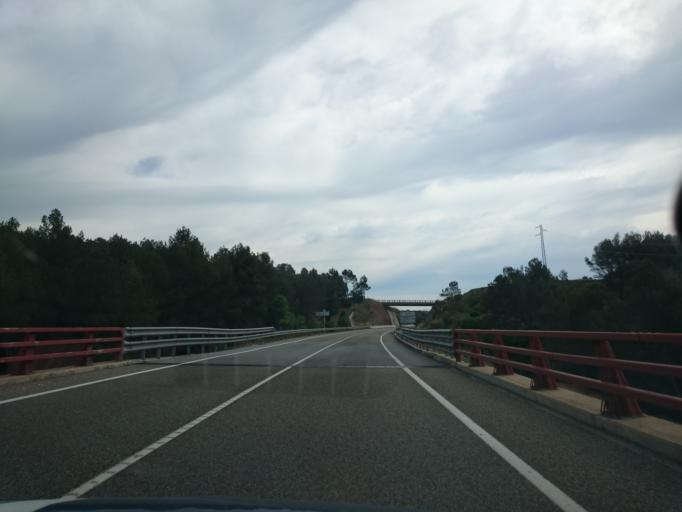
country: ES
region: Catalonia
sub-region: Provincia de Barcelona
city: Sant Salvador de Guardiola
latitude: 41.6892
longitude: 1.7618
